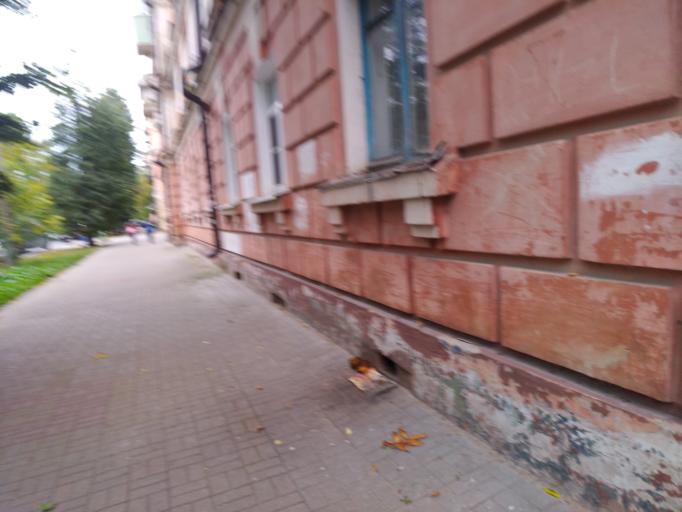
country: RU
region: Kaluga
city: Kaluga
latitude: 54.5307
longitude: 36.2588
